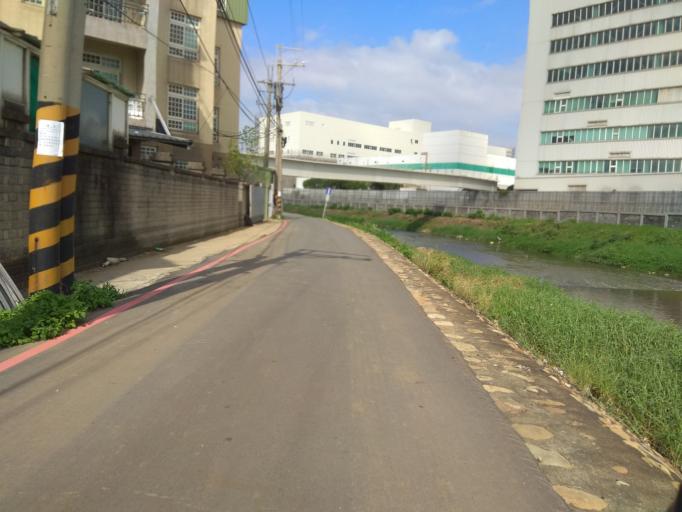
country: TW
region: Taiwan
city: Taoyuan City
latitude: 25.0638
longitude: 121.2190
